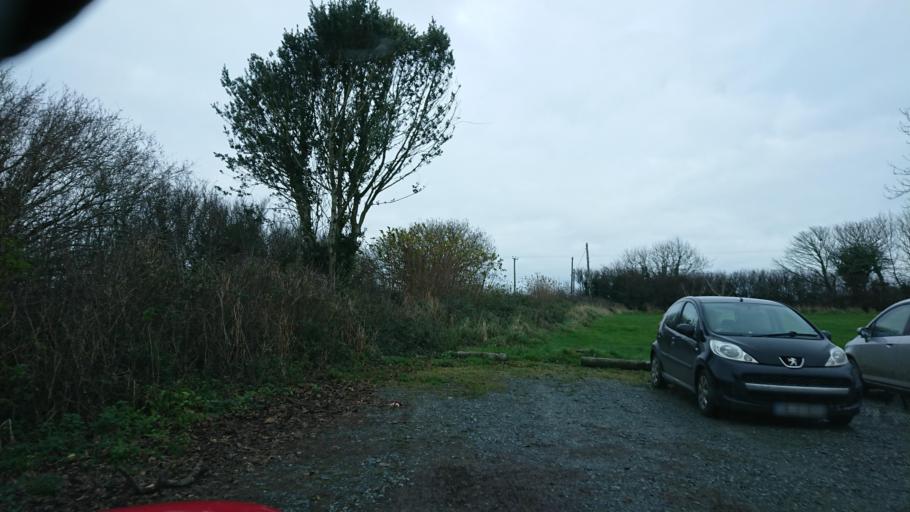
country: GB
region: England
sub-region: Cornwall
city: Fowey
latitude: 50.3376
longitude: -4.5681
